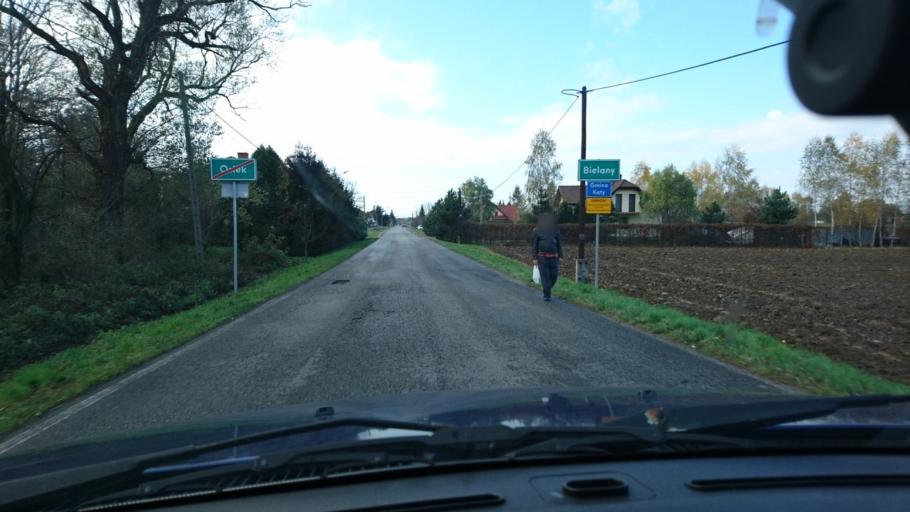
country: PL
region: Lesser Poland Voivodeship
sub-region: Powiat oswiecimski
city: Malec
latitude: 49.9405
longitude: 19.2190
